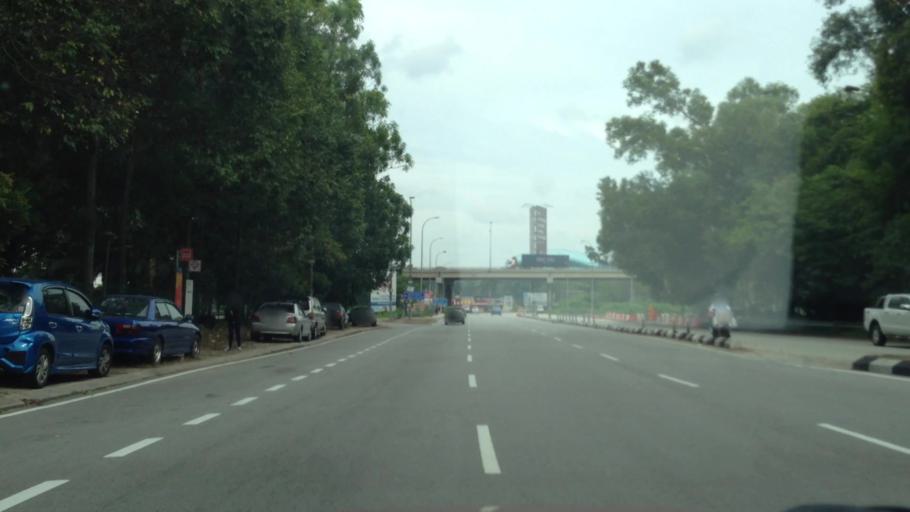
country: MY
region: Selangor
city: Shah Alam
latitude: 3.0807
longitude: 101.5540
